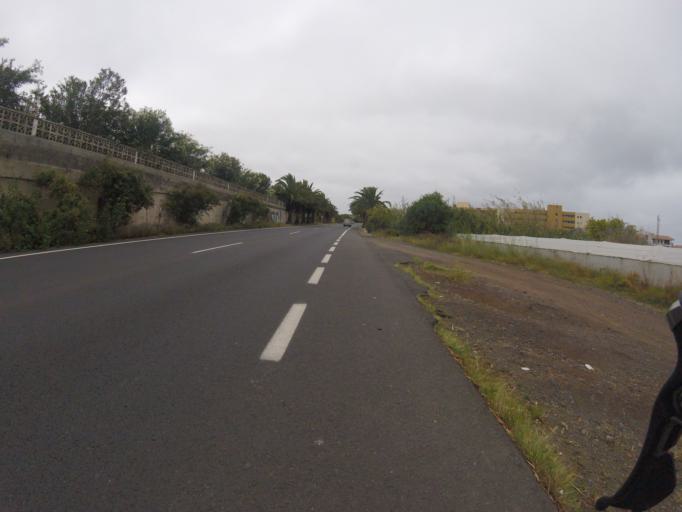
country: ES
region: Canary Islands
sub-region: Provincia de Santa Cruz de Tenerife
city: Tegueste
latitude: 28.5451
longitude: -16.3514
